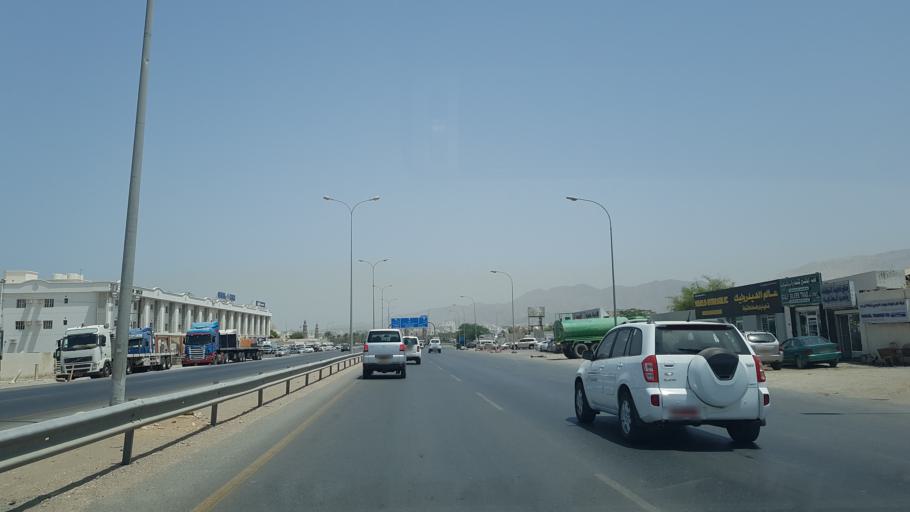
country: OM
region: Muhafazat Masqat
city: Bawshar
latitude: 23.5824
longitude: 58.3772
